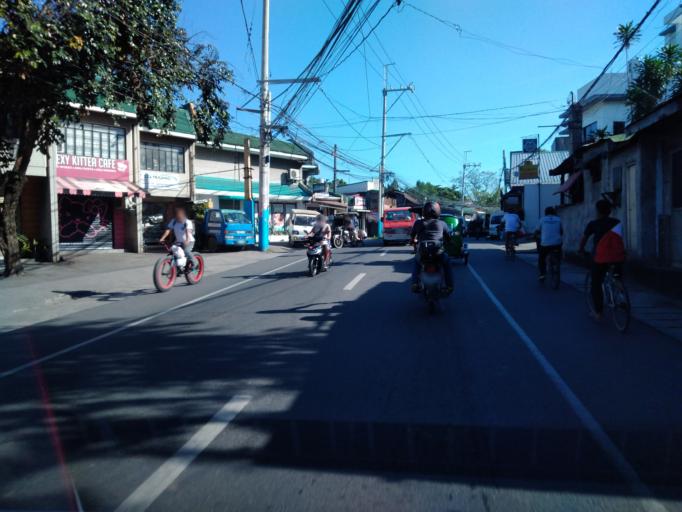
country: PH
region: Central Luzon
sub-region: Province of Bulacan
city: Meycauayan
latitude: 14.7411
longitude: 120.9683
